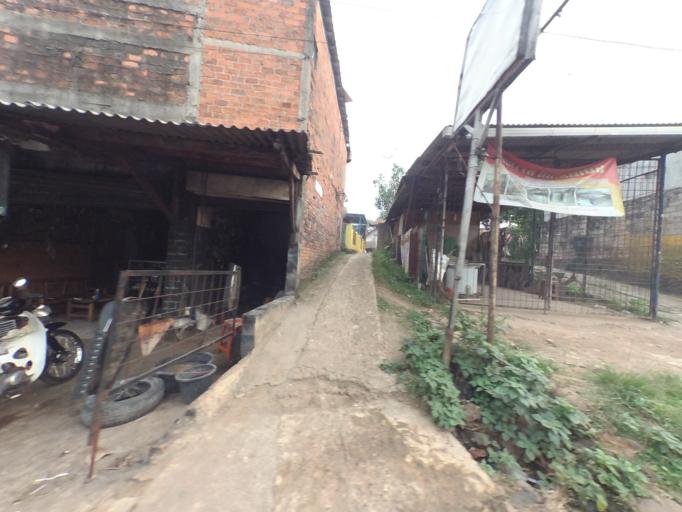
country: ID
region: West Java
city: Ciampea
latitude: -6.5629
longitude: 106.6830
